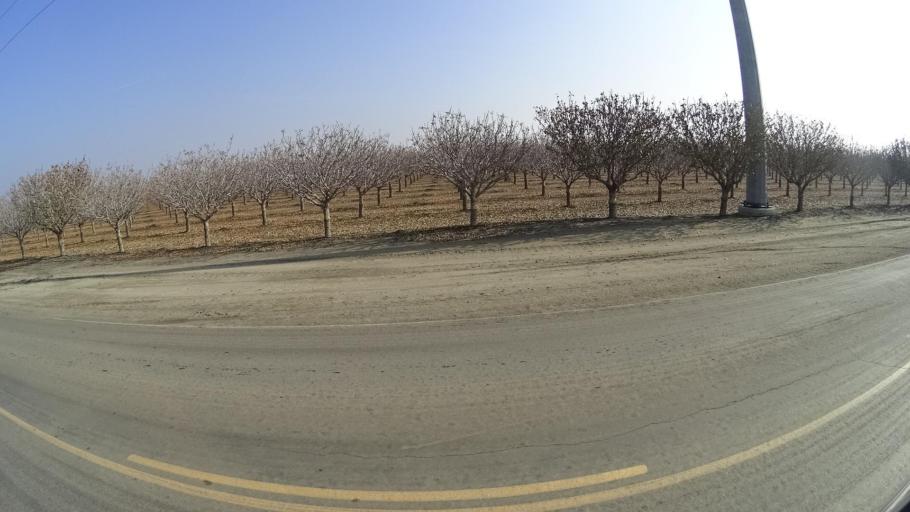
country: US
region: California
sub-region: Kern County
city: Buttonwillow
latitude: 35.3569
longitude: -119.4477
